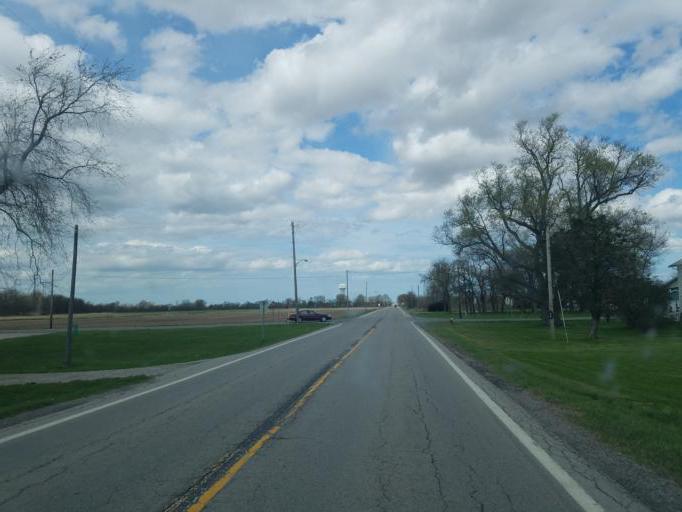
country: US
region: Ohio
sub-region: Huron County
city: Bellevue
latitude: 41.3242
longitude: -82.7670
